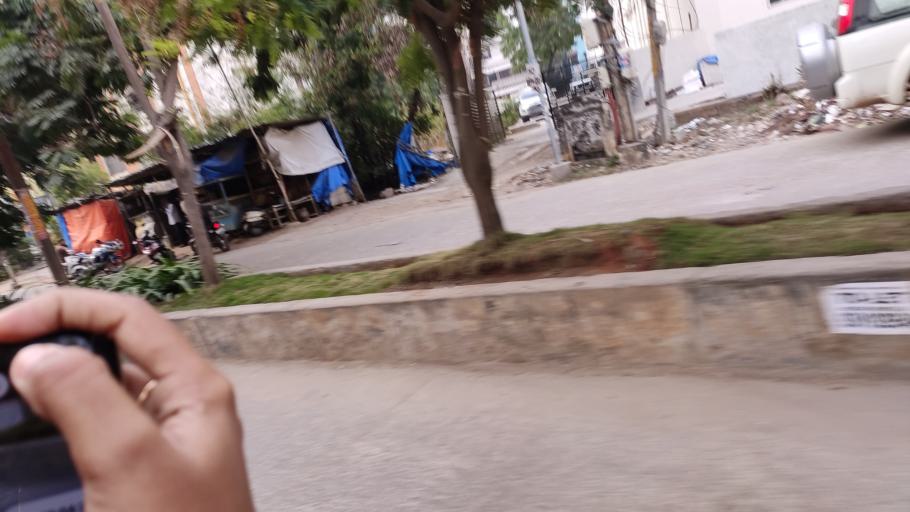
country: IN
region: Telangana
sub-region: Rangareddi
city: Kukatpalli
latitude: 17.4871
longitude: 78.3882
